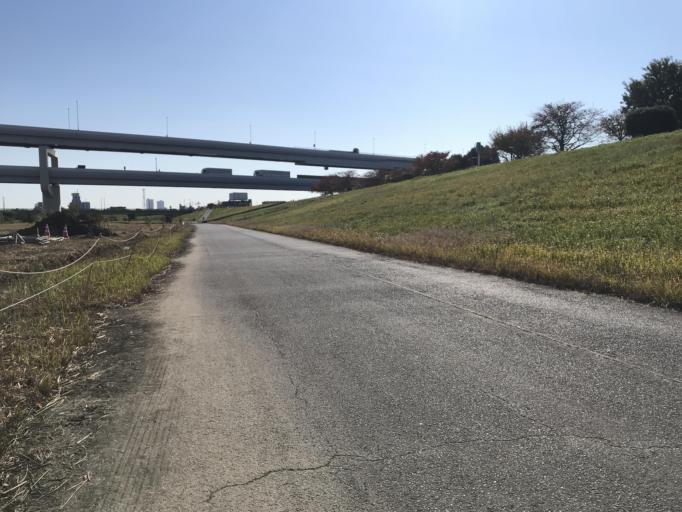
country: JP
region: Saitama
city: Kawaguchi
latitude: 35.7662
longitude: 139.7576
